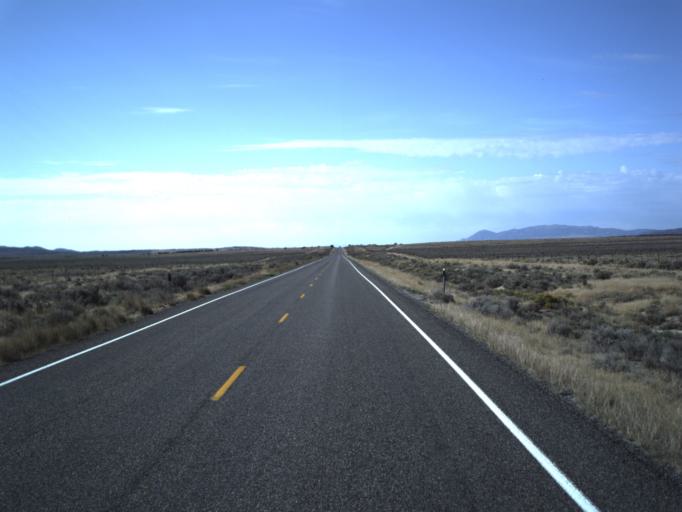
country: US
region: Idaho
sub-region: Cassia County
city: Burley
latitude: 41.7429
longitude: -113.5186
